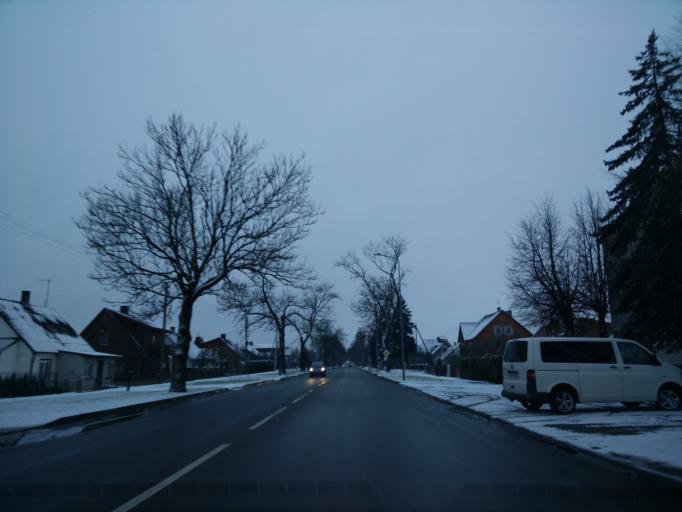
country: LT
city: Kelme
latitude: 55.6275
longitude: 22.9270
